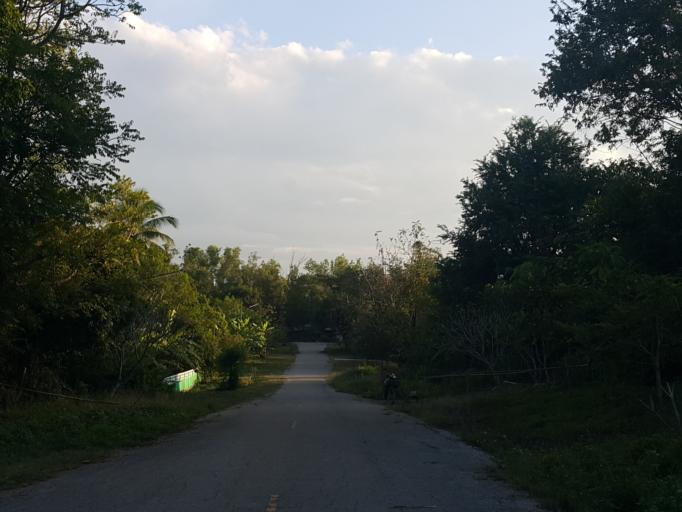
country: TH
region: Lampang
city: Lampang
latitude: 18.4411
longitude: 99.5718
